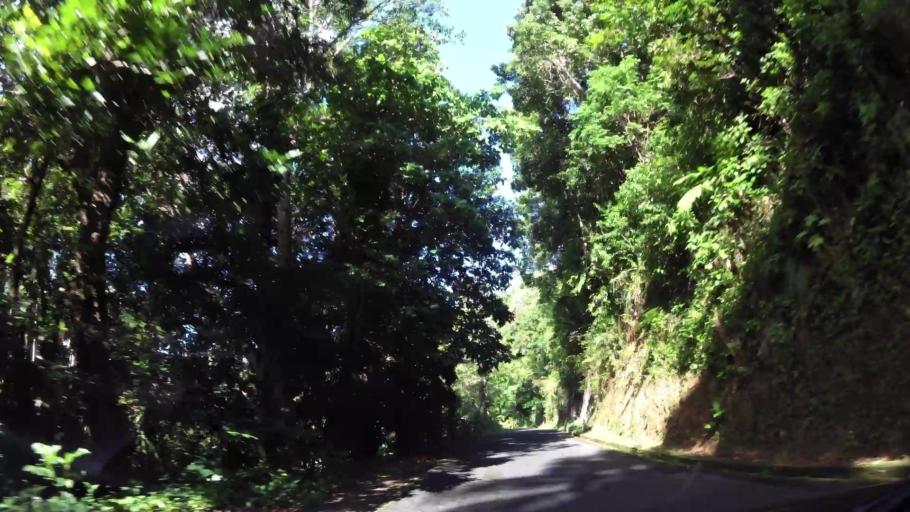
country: DM
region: Saint Andrew
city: Calibishie
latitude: 15.5893
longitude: -61.3974
